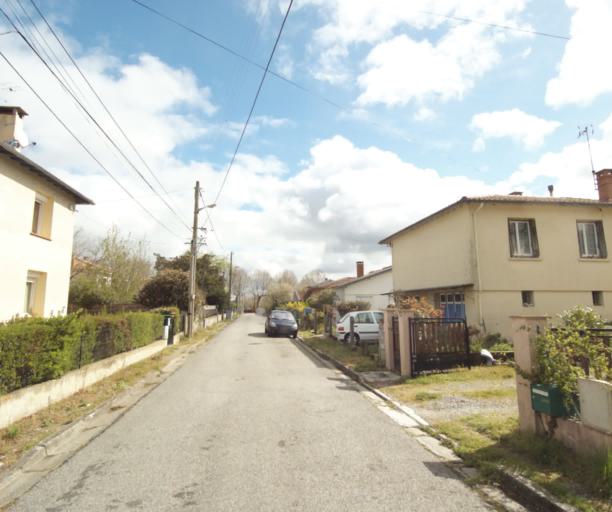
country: FR
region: Midi-Pyrenees
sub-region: Departement de l'Ariege
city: Saverdun
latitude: 43.2381
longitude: 1.5704
